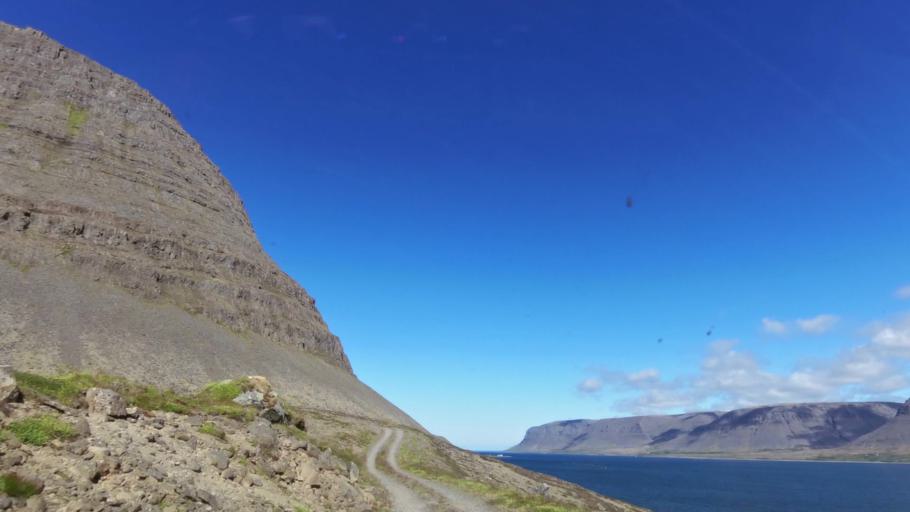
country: IS
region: West
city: Olafsvik
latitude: 65.6253
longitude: -23.8966
